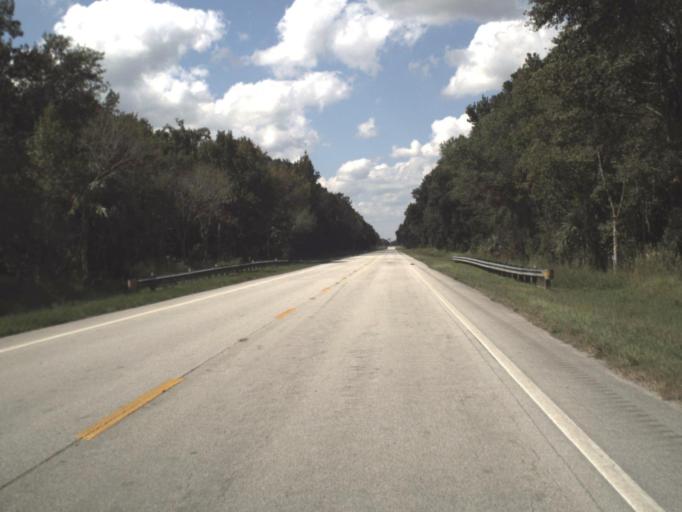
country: US
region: Florida
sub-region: Highlands County
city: Sebring
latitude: 27.4124
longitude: -81.5433
